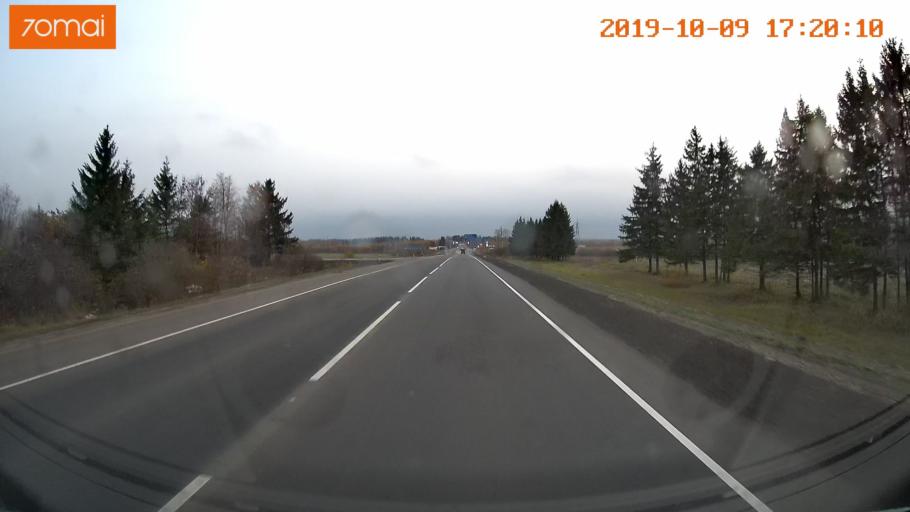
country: RU
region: Ivanovo
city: Furmanov
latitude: 57.2376
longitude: 41.1444
